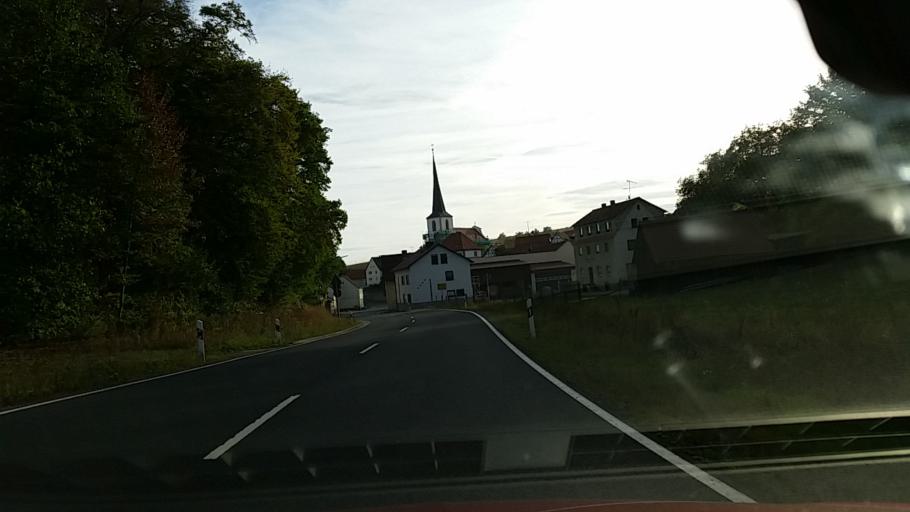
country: DE
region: Bavaria
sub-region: Regierungsbezirk Unterfranken
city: Stockheim
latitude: 50.4664
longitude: 10.3221
